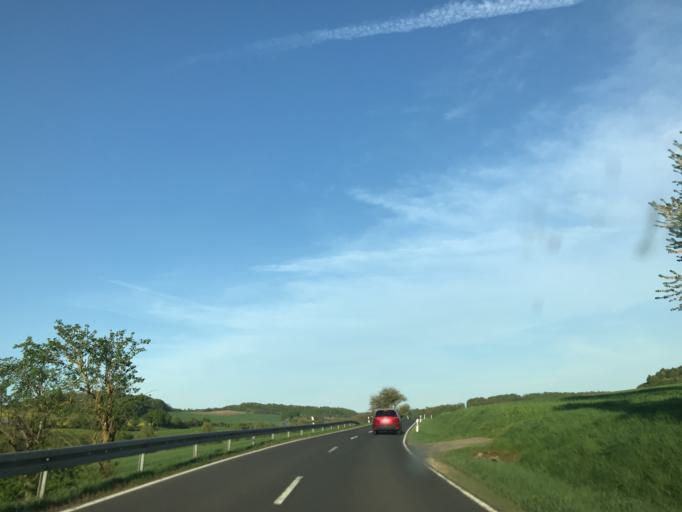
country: DE
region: Thuringia
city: Geisleden
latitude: 51.3437
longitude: 10.2131
